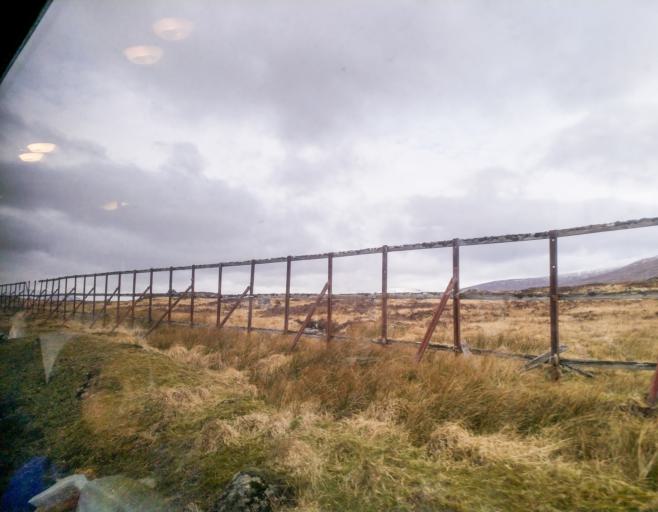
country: GB
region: Scotland
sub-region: Highland
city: Spean Bridge
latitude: 56.7020
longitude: -4.5799
